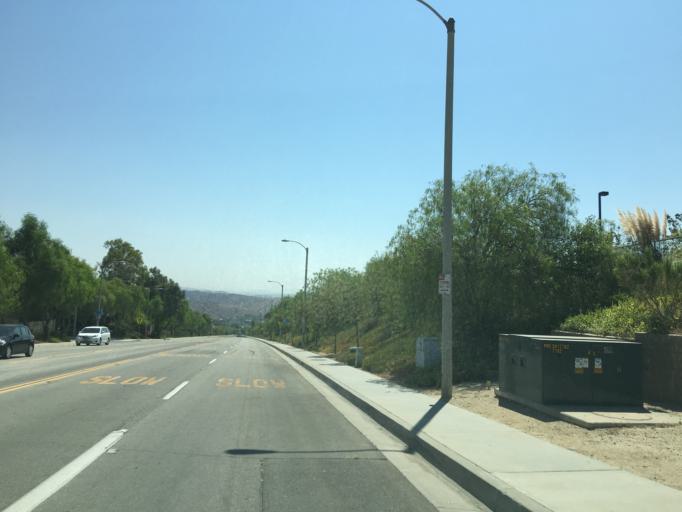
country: US
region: California
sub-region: Los Angeles County
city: Castaic
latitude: 34.4726
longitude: -118.6411
